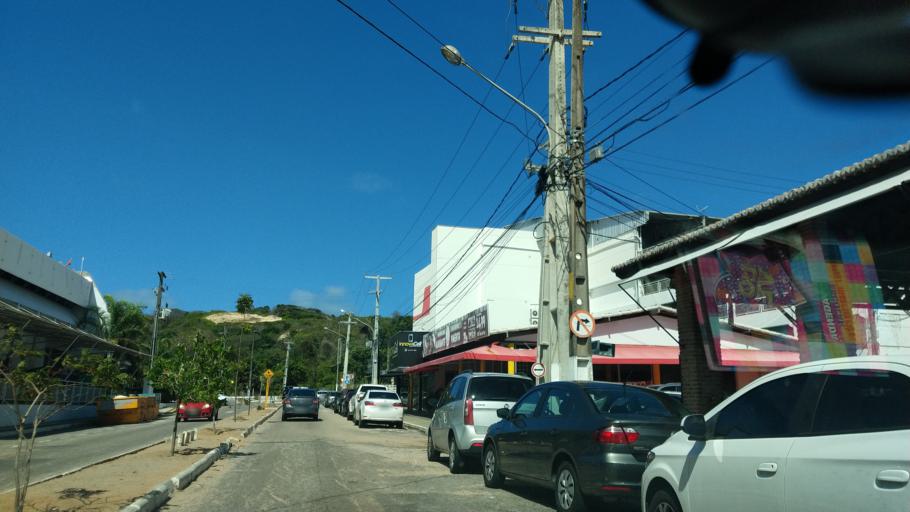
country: BR
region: Rio Grande do Norte
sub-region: Natal
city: Natal
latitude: -5.8671
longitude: -35.1853
